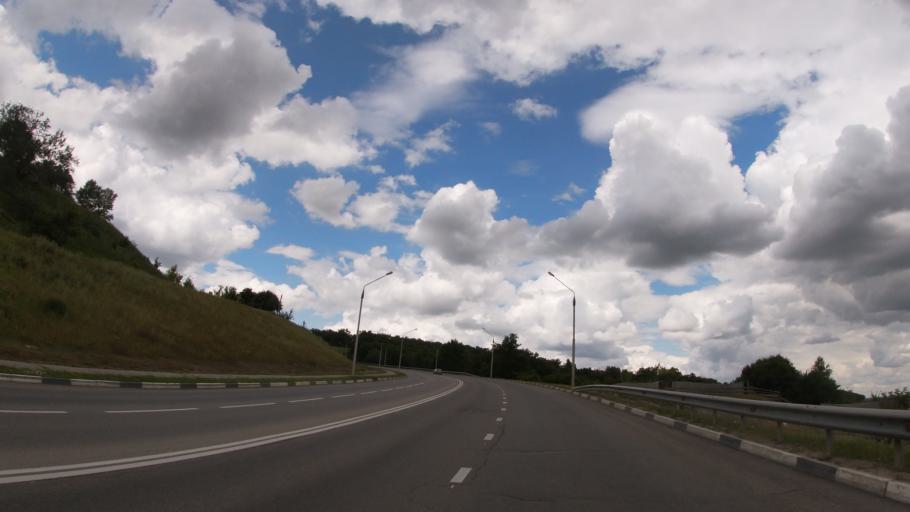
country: RU
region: Belgorod
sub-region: Belgorodskiy Rayon
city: Belgorod
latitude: 50.6194
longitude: 36.6164
